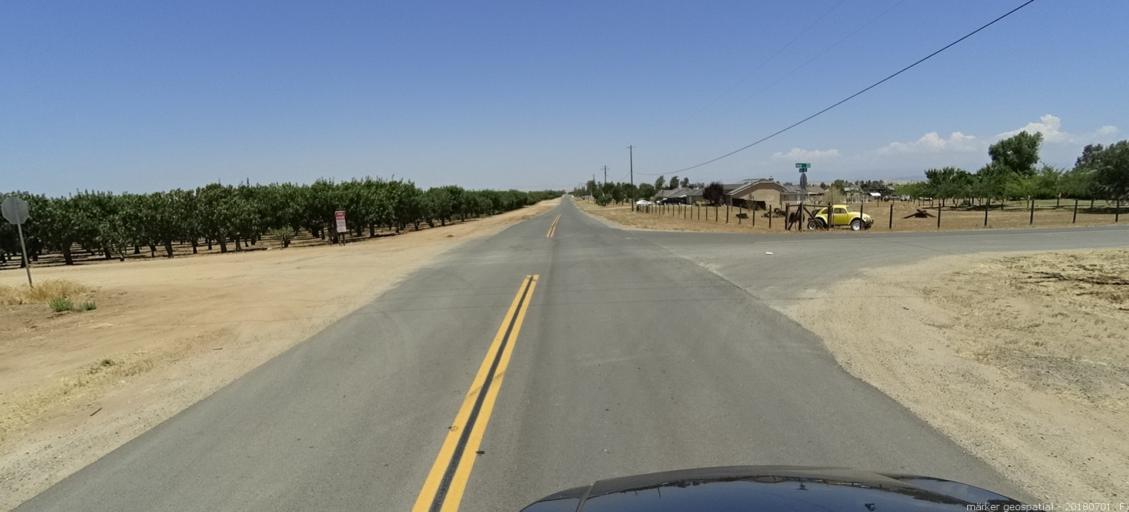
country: US
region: California
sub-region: Madera County
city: Madera Acres
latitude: 37.0396
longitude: -120.0017
